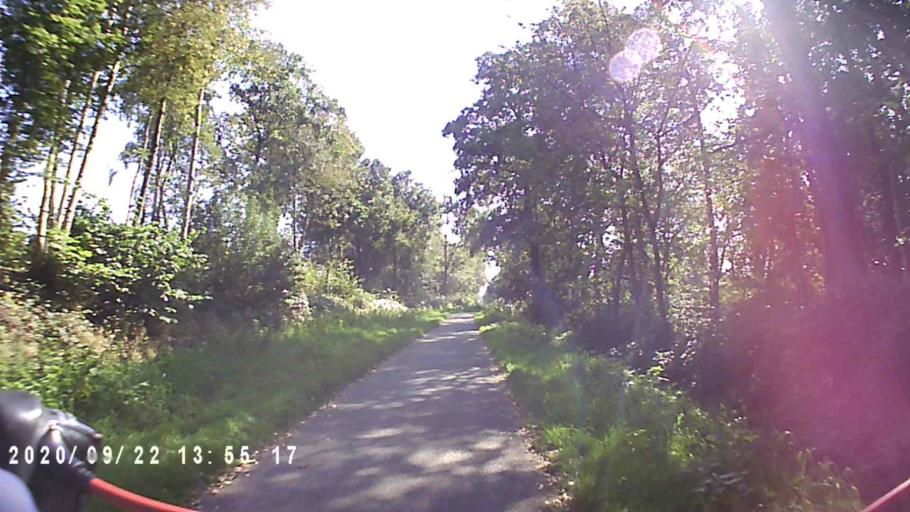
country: NL
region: Groningen
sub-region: Gemeente Leek
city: Leek
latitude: 53.1264
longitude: 6.4201
